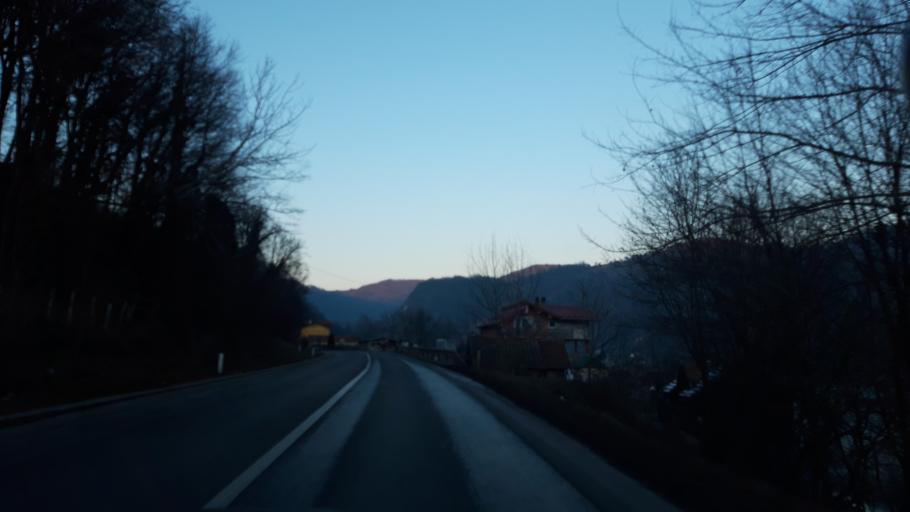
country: RS
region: Central Serbia
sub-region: Macvanski Okrug
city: Mali Zvornik
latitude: 44.3269
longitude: 19.1271
